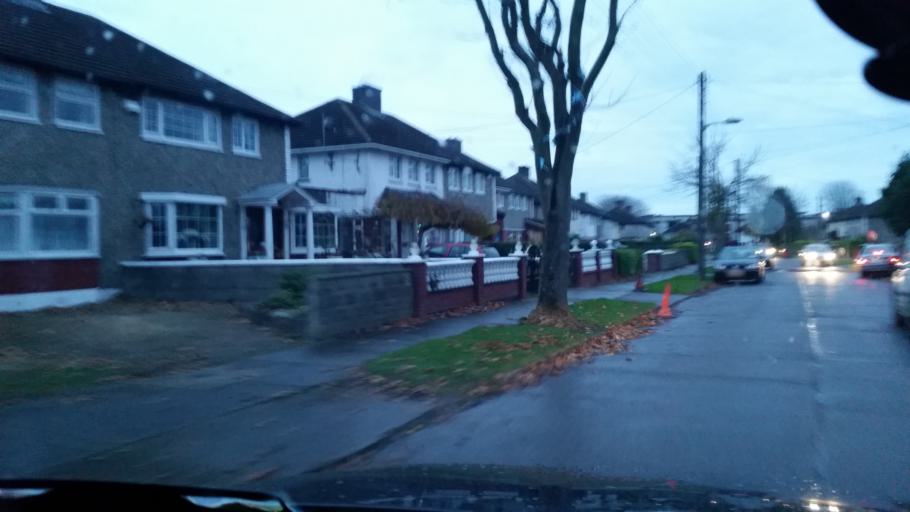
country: IE
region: Leinster
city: Glasnevin
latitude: 53.3892
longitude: -6.2605
